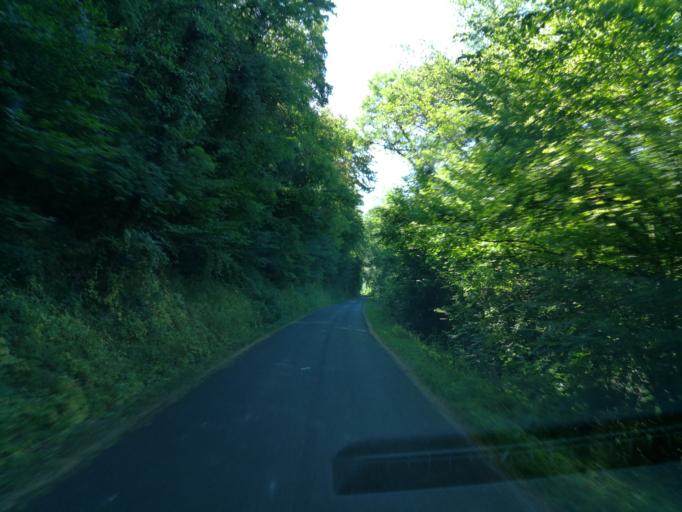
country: FR
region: Midi-Pyrenees
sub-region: Departement du Lot
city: Souillac
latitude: 44.8749
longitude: 1.4032
